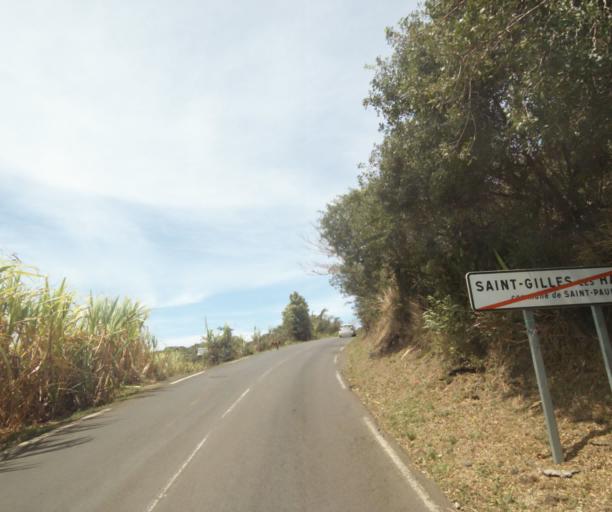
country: RE
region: Reunion
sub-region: Reunion
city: Saint-Paul
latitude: -21.0488
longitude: 55.2766
